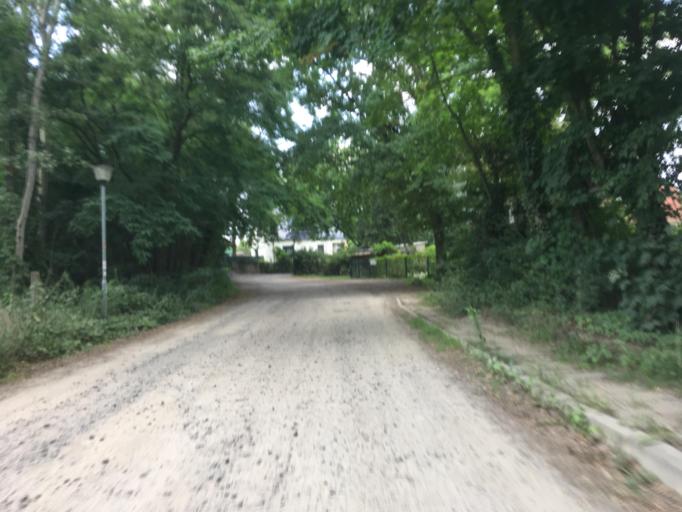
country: DE
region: Brandenburg
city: Wildau
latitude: 52.3401
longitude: 13.6252
